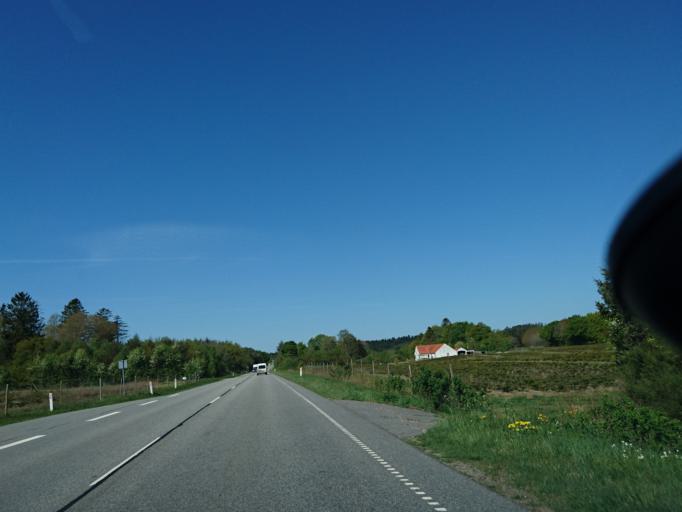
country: DK
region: North Denmark
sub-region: Hjorring Kommune
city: Sindal
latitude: 57.4575
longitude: 10.3384
